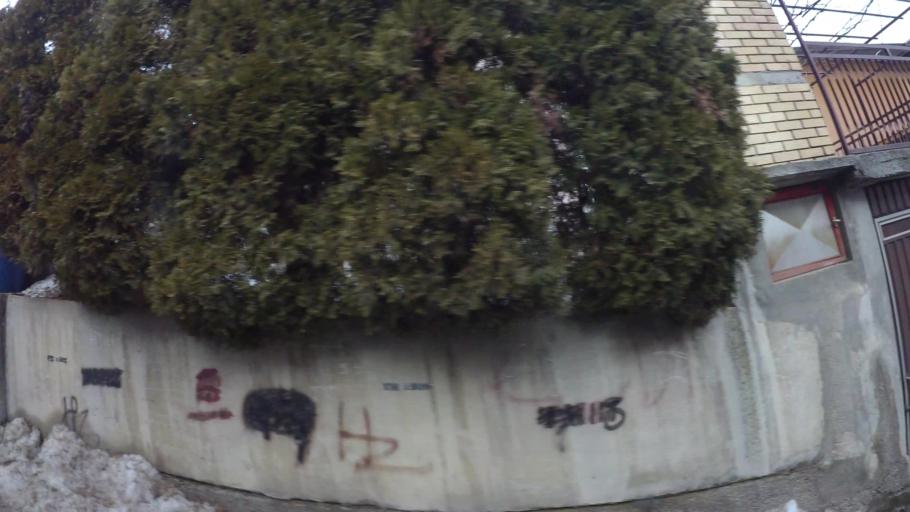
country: BA
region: Federation of Bosnia and Herzegovina
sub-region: Kanton Sarajevo
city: Sarajevo
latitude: 43.8598
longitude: 18.3450
